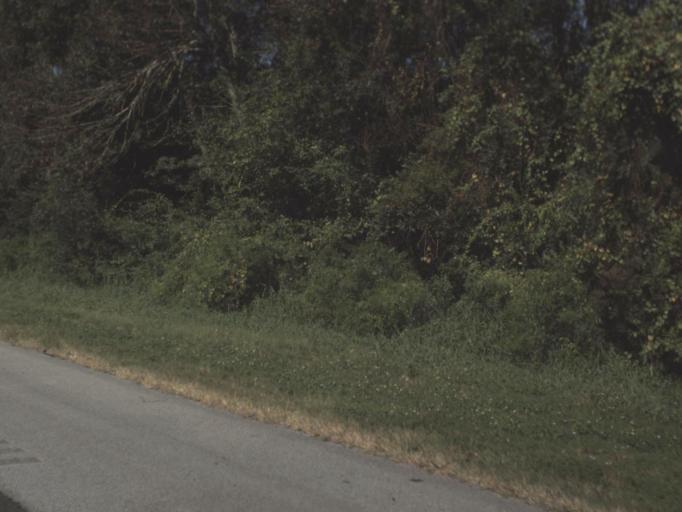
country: US
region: Florida
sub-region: Sumter County
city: Wildwood
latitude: 28.8445
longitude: -82.0672
